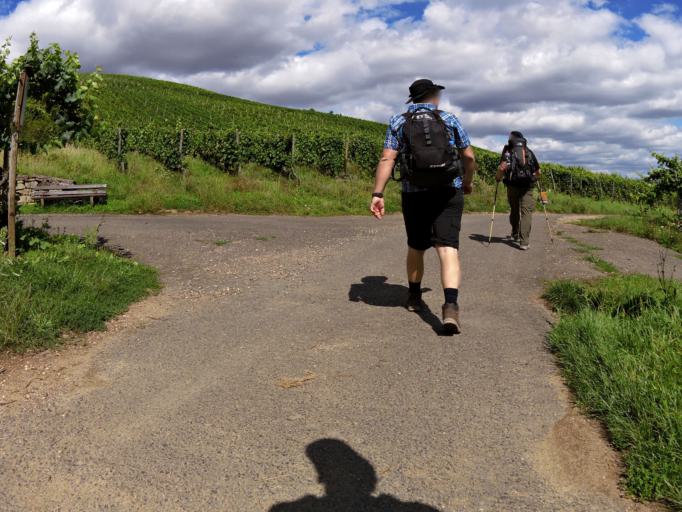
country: DE
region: Rheinland-Pfalz
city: Niederhausen
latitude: 49.7977
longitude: 7.7760
